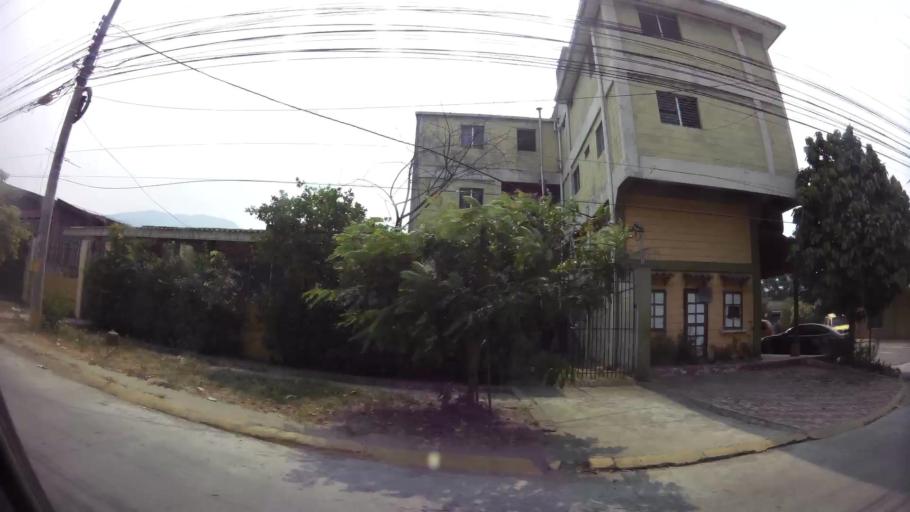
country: HN
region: Cortes
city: San Pedro Sula
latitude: 15.4880
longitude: -88.0329
